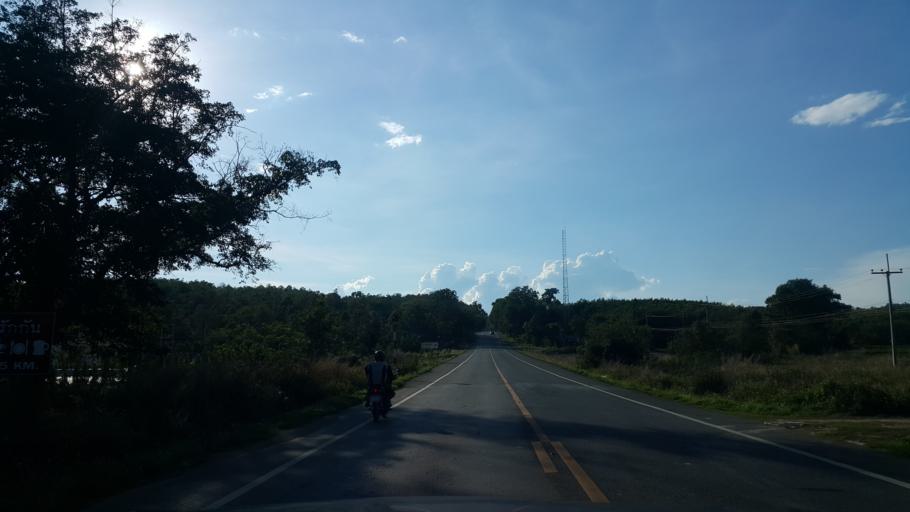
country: TH
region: Lampang
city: Wang Nuea
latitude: 19.1205
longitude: 99.6729
